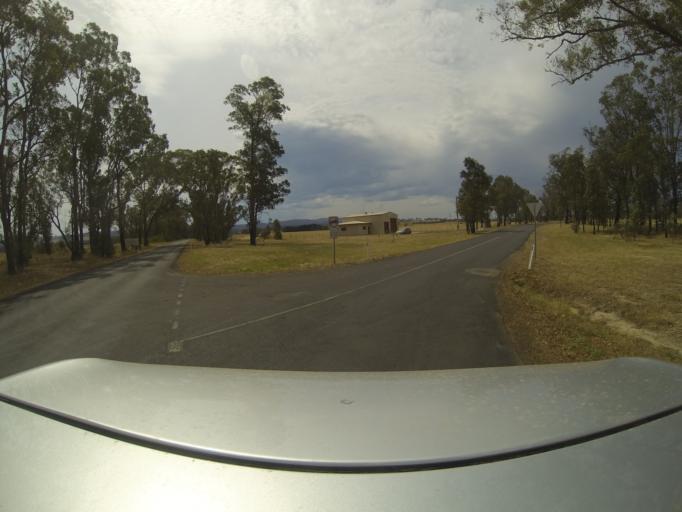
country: AU
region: Victoria
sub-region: Wellington
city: Heyfield
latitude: -37.9413
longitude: 146.6990
